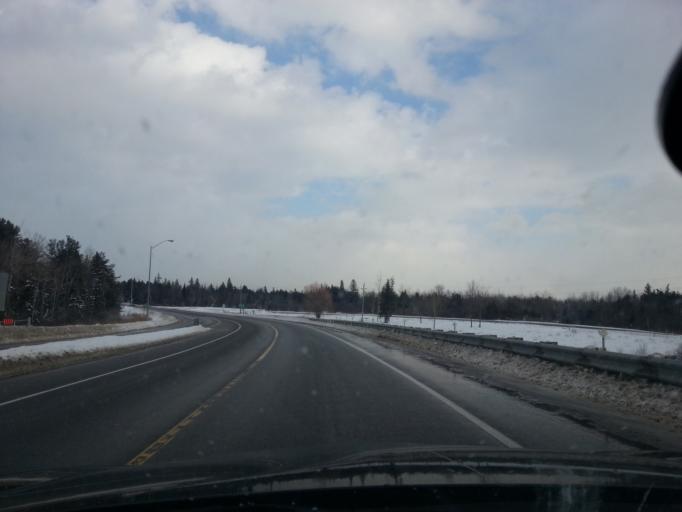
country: CA
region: Ontario
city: Bells Corners
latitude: 45.2493
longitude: -75.9666
